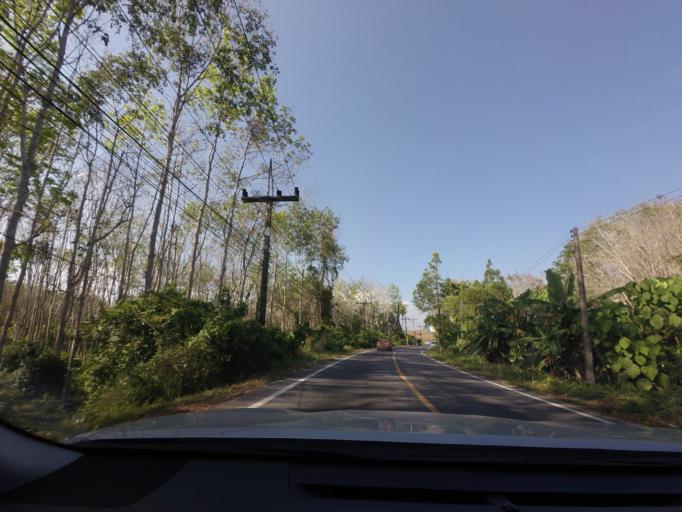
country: TH
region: Phangnga
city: Takua Thung
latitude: 8.2670
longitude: 98.3717
